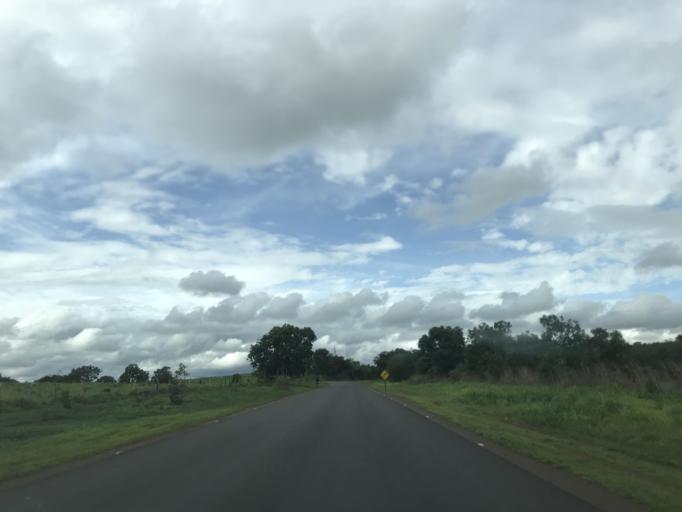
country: BR
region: Goias
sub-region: Bela Vista De Goias
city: Bela Vista de Goias
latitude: -17.0423
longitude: -48.6634
